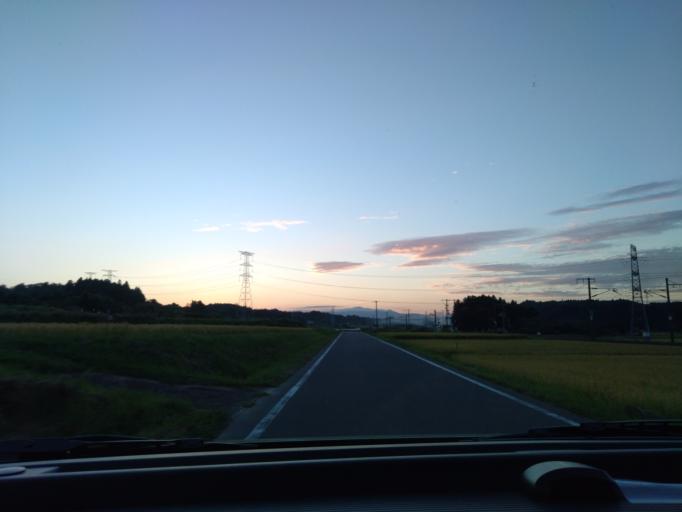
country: JP
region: Iwate
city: Ichinoseki
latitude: 38.8573
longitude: 141.1448
